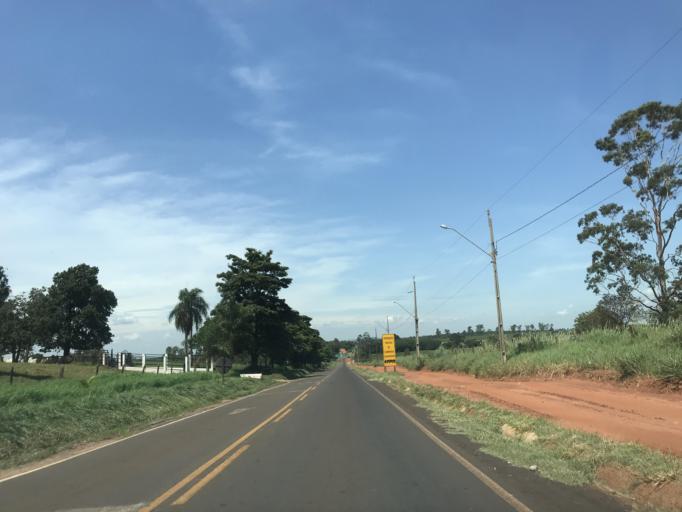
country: BR
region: Parana
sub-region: Paranavai
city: Nova Aurora
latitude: -22.9484
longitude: -52.6985
